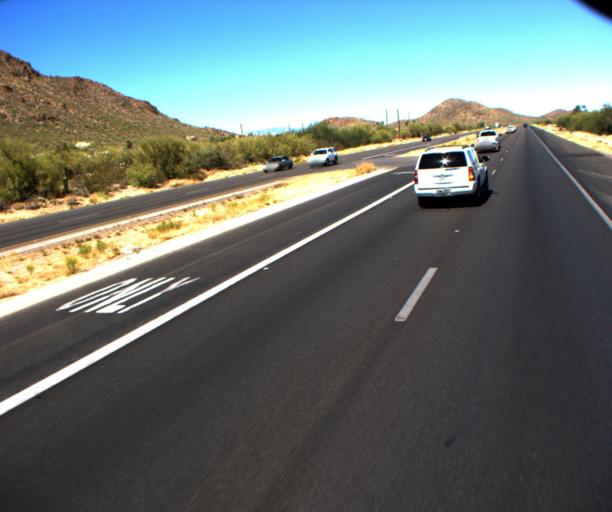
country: US
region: Arizona
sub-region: Pima County
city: Tucson Estates
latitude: 32.1746
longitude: -111.0591
